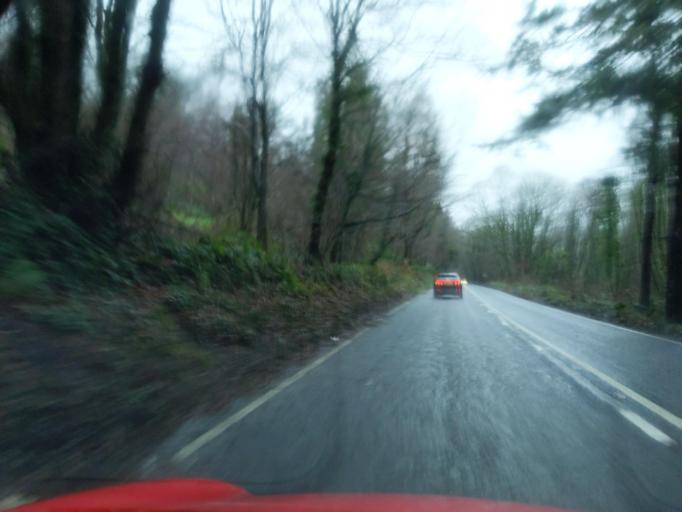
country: GB
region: England
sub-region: Cornwall
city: South Hill
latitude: 50.5588
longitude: -4.3304
